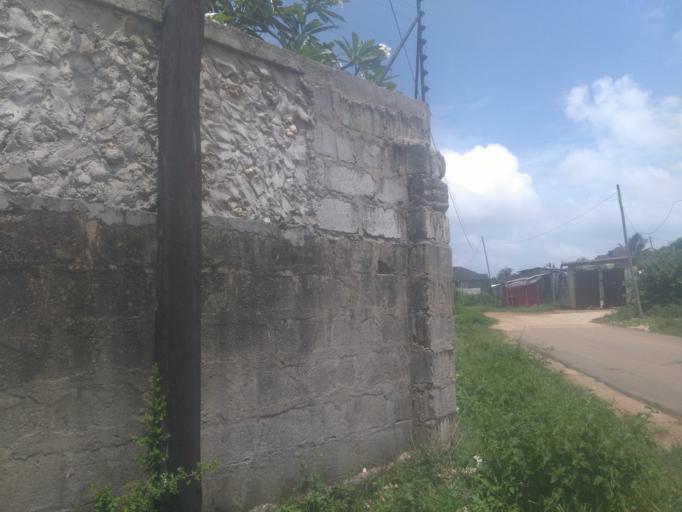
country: TZ
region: Zanzibar Urban/West
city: Zanzibar
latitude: -6.2134
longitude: 39.2056
